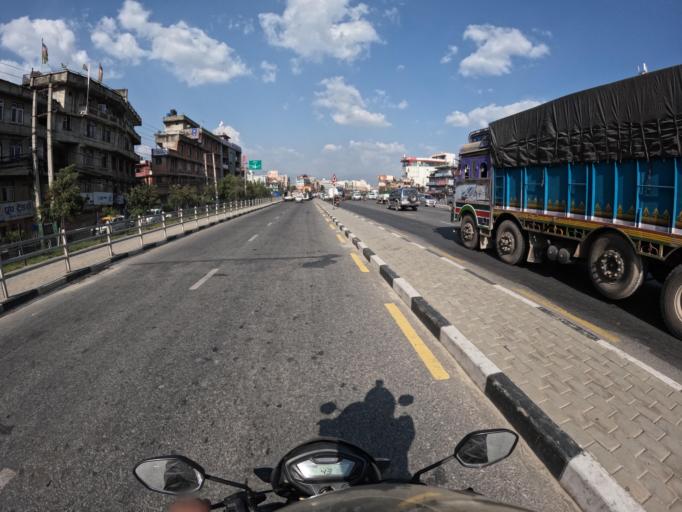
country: NP
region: Central Region
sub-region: Bagmati Zone
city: Patan
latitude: 27.6660
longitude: 85.3314
